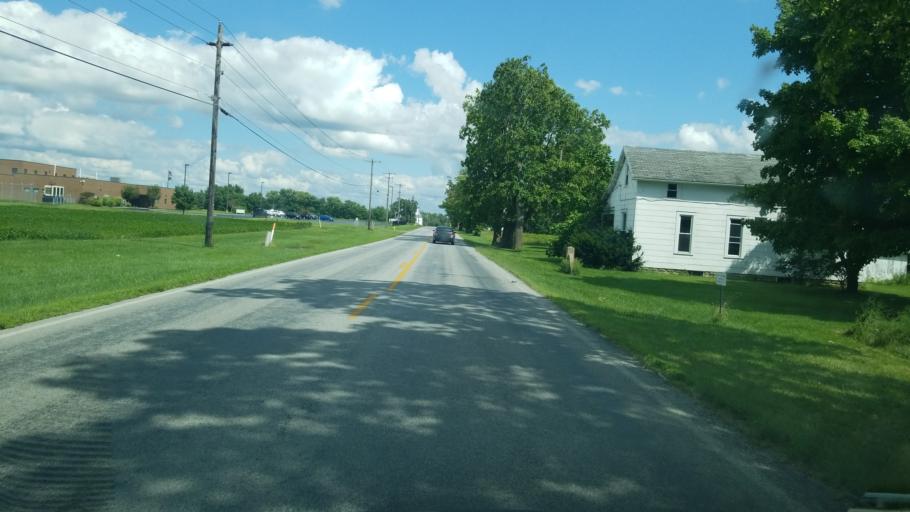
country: US
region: Ohio
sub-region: Allen County
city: Lima
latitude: 40.7883
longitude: -84.1053
